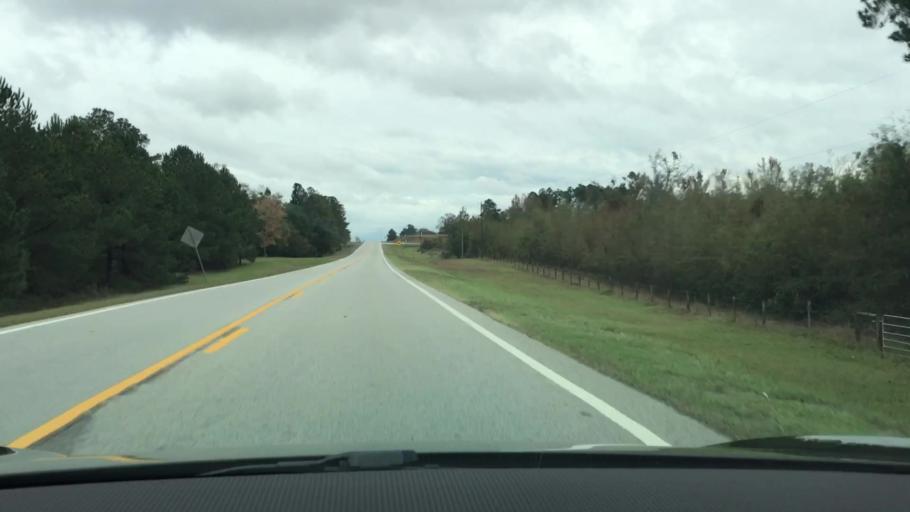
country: US
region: Georgia
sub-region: Jefferson County
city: Wrens
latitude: 33.2625
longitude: -82.4819
